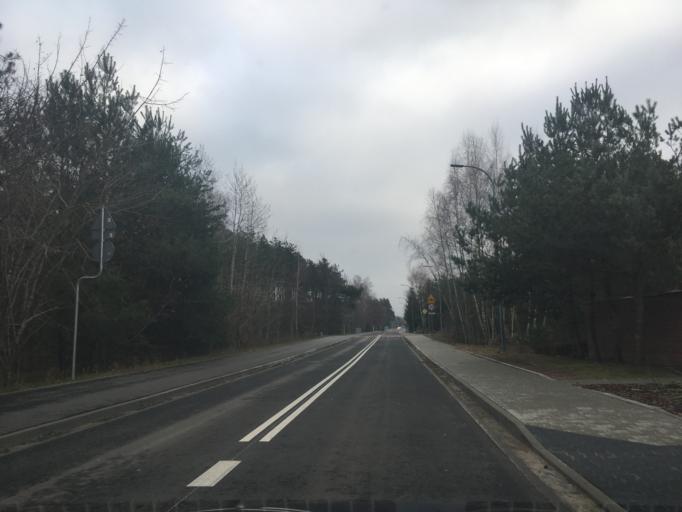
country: PL
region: Masovian Voivodeship
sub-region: Powiat piaseczynski
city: Lesznowola
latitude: 52.0653
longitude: 20.9747
